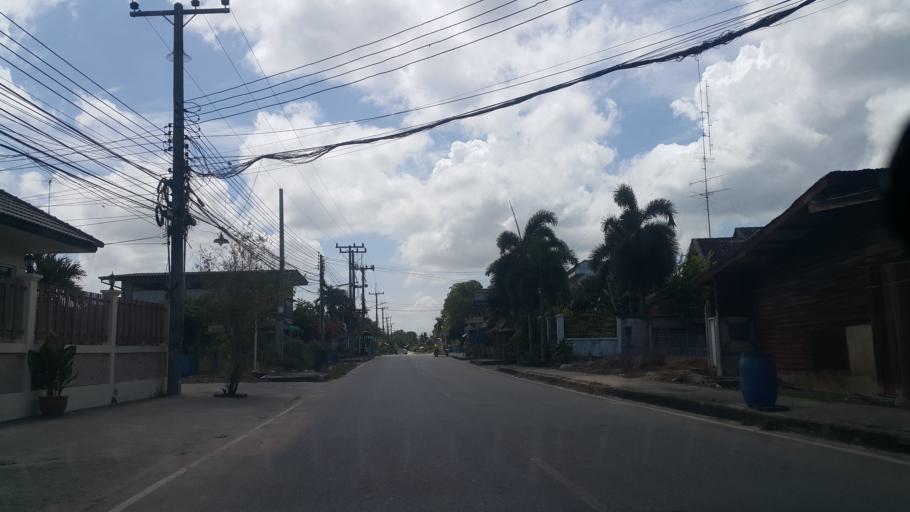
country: TH
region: Rayong
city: Ban Chang
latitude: 12.7943
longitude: 101.0299
